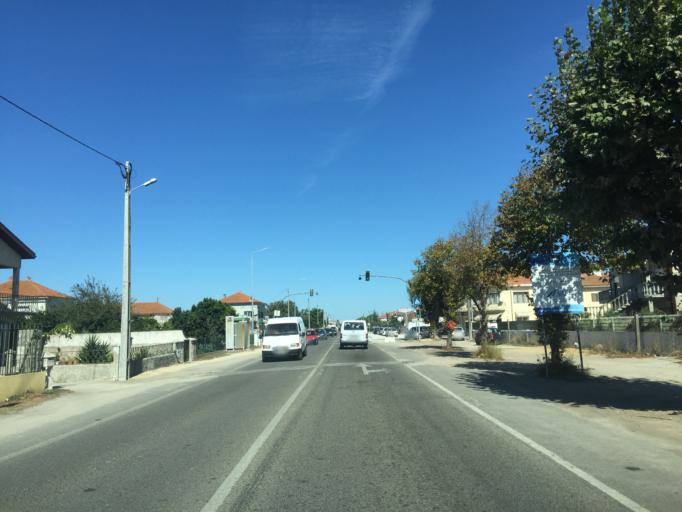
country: PT
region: Coimbra
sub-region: Montemor-O-Velho
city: Arazede
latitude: 40.3055
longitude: -8.7577
